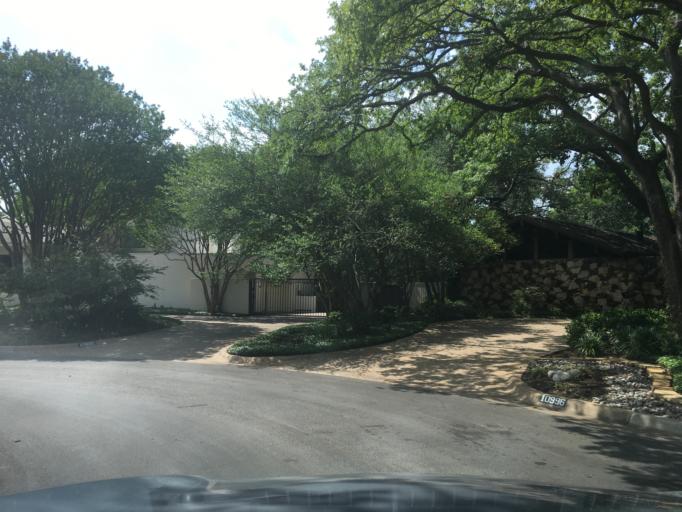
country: US
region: Texas
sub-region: Dallas County
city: University Park
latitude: 32.8983
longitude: -96.8220
